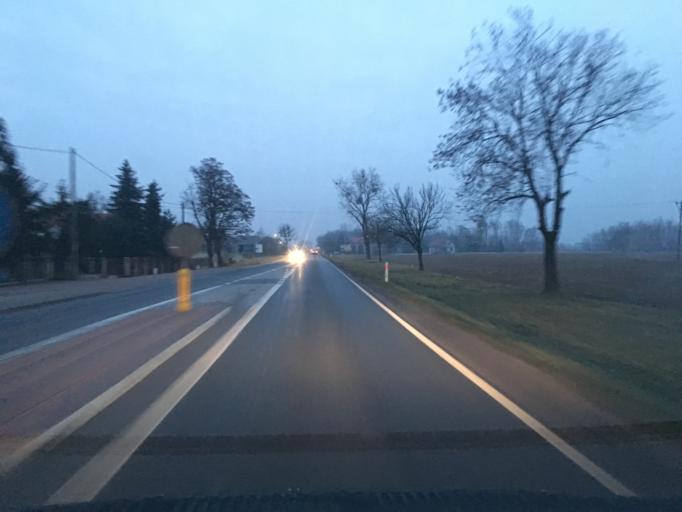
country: PL
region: Lower Silesian Voivodeship
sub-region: Powiat olawski
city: Wierzbno
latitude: 50.9829
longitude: 17.2246
